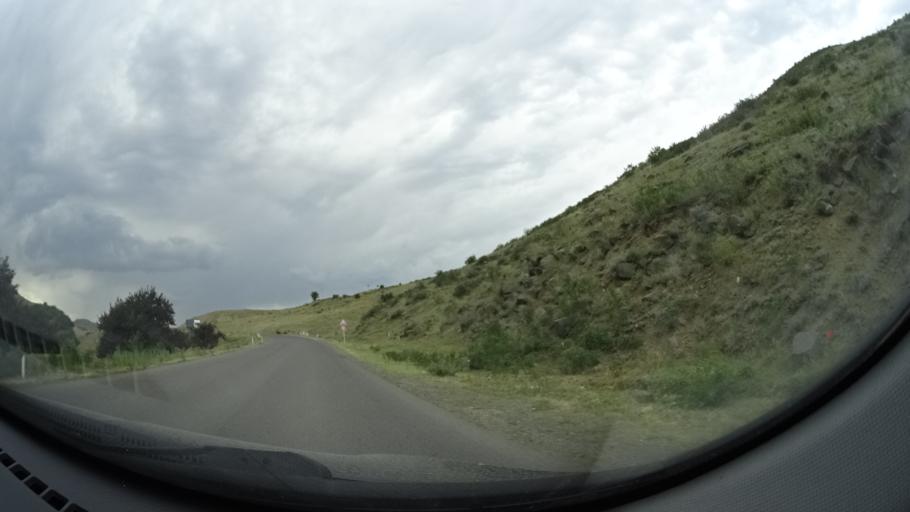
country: GE
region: Samtskhe-Javakheti
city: Aspindza
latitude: 41.5990
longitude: 43.1521
